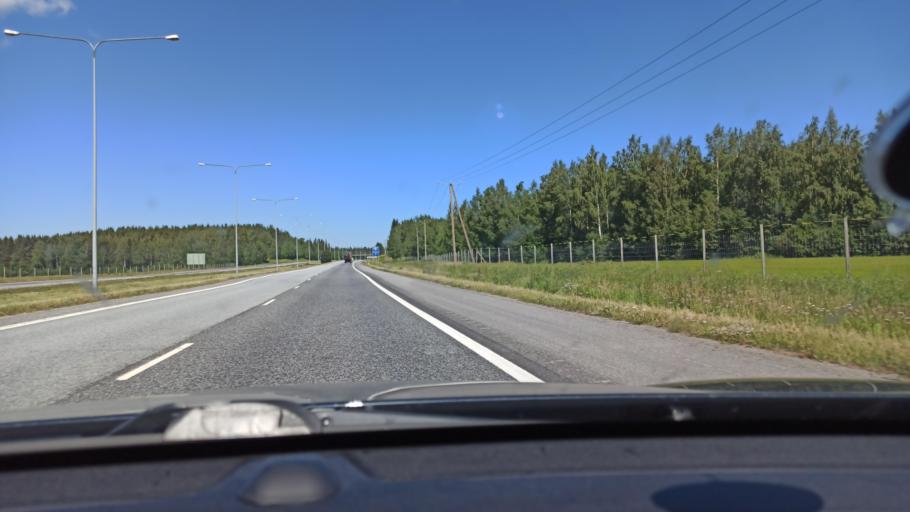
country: FI
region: Ostrobothnia
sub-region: Vaasa
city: Ristinummi
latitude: 63.0467
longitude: 21.7229
